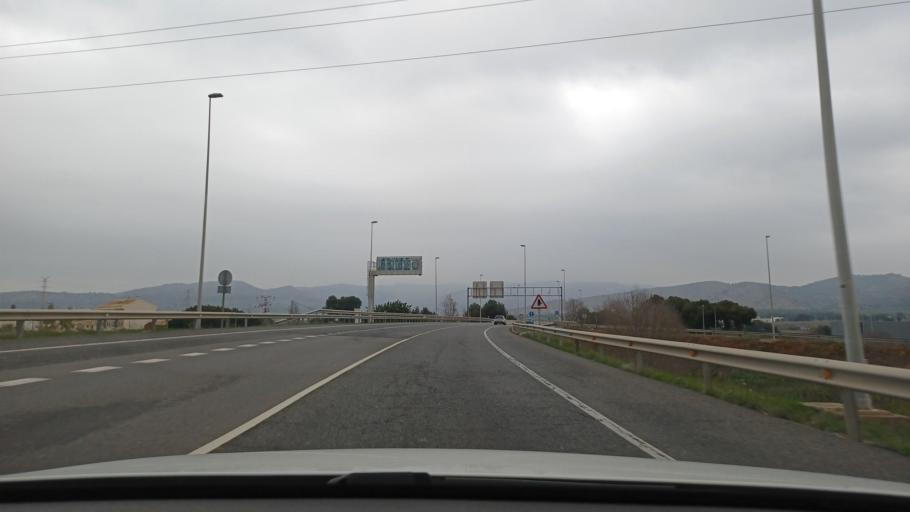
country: ES
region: Valencia
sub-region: Provincia de Castello
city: Borriol
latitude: 39.9923
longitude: -0.0897
